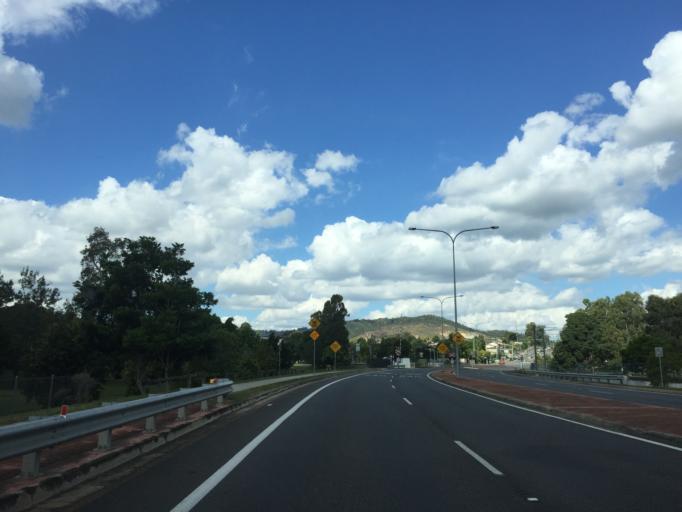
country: AU
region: Queensland
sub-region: Moreton Bay
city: Ferny Hills
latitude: -27.4038
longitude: 152.9390
